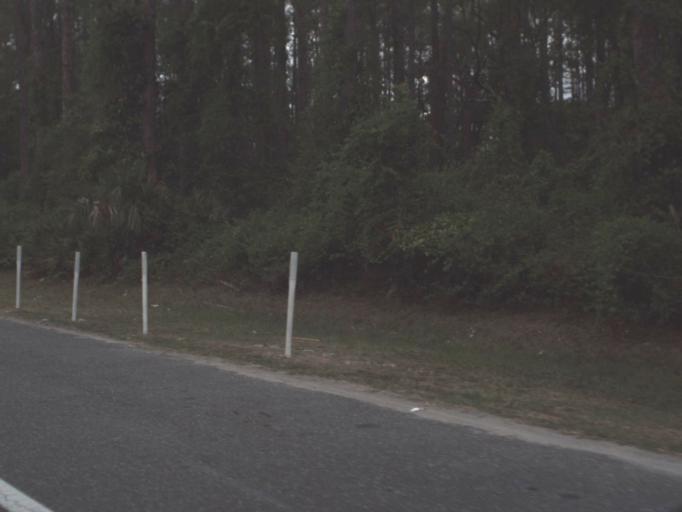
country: US
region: Florida
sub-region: Marion County
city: Ocala
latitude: 29.2202
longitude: -82.0338
